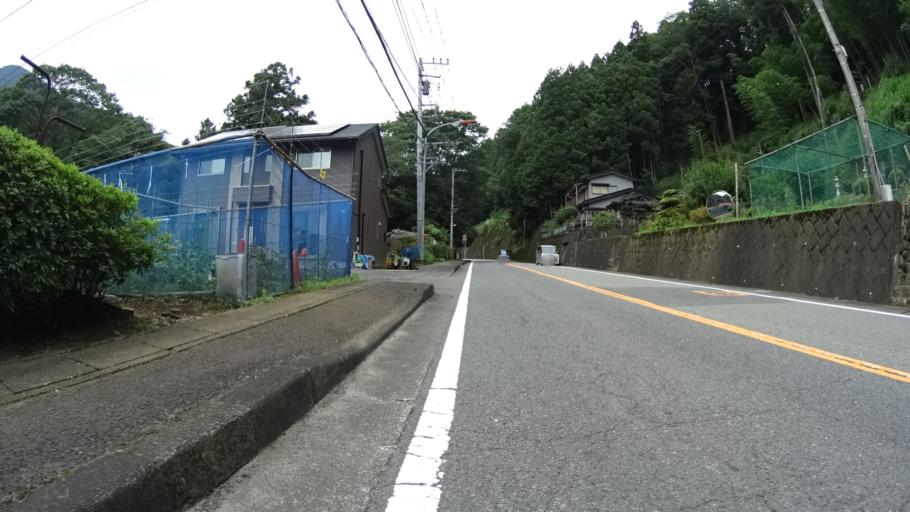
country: JP
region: Kanagawa
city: Atsugi
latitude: 35.4927
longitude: 139.2690
